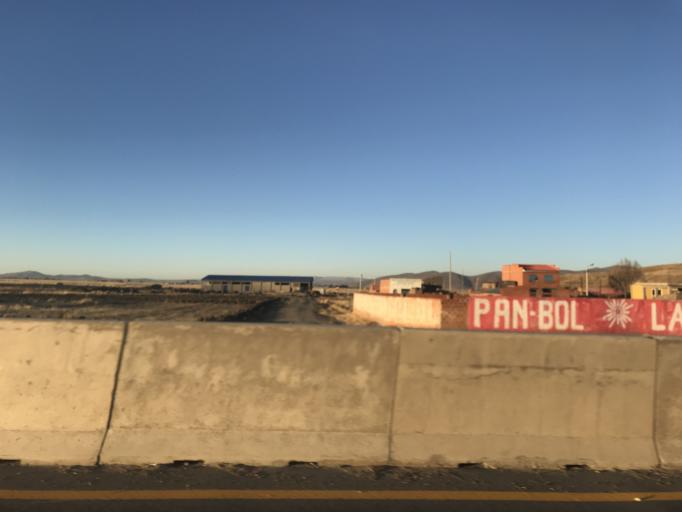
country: BO
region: La Paz
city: Batallas
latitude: -16.2983
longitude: -68.5232
